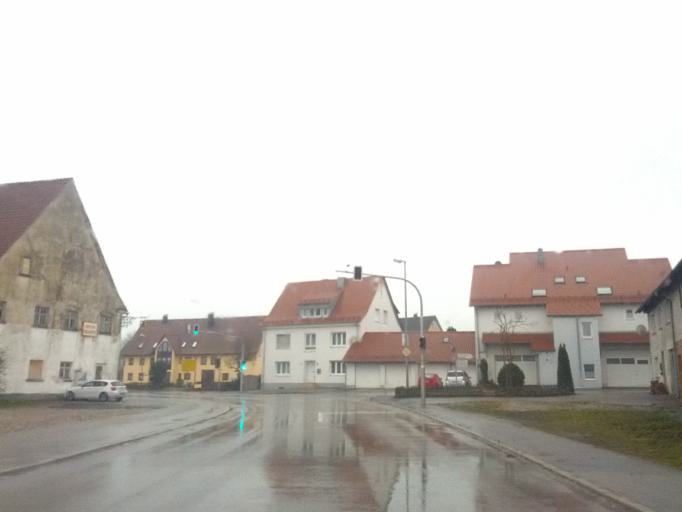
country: DE
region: Baden-Wuerttemberg
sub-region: Tuebingen Region
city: Erlenmoos
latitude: 48.0639
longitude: 9.9742
